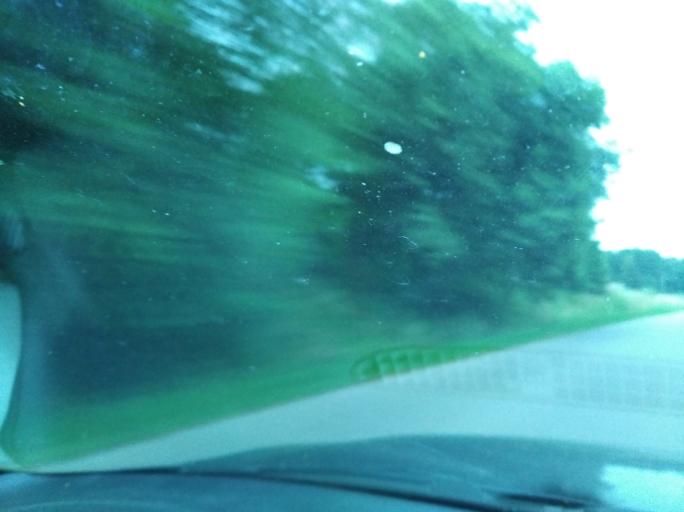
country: PL
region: Subcarpathian Voivodeship
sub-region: Powiat ropczycko-sedziszowski
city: Zagorzyce
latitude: 49.9923
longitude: 21.7167
